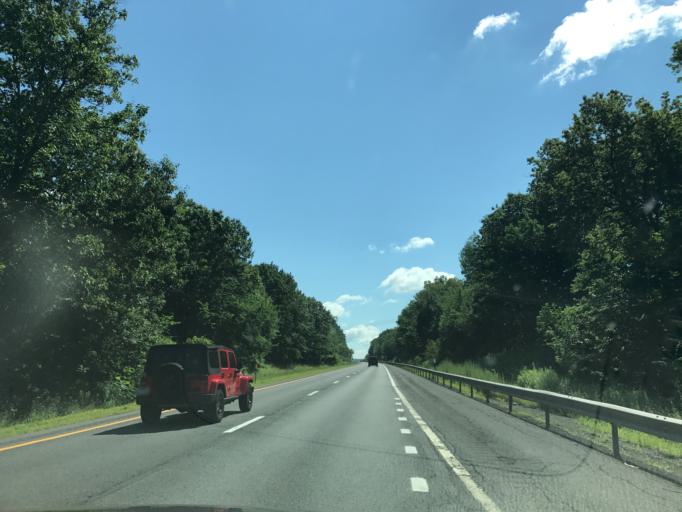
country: US
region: New York
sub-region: Columbia County
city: Niverville
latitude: 42.4819
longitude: -73.6660
